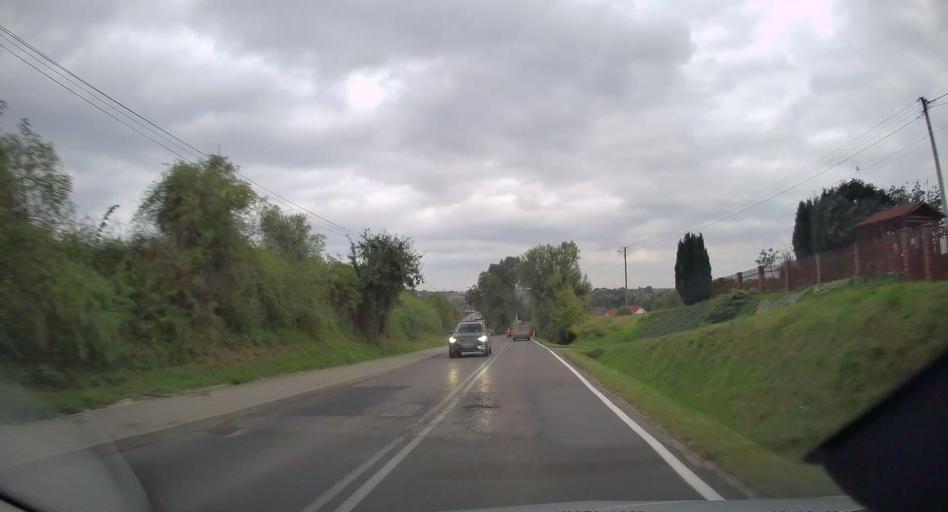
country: PL
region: Lesser Poland Voivodeship
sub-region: Powiat krakowski
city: Slomniki
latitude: 50.1554
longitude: 20.1047
